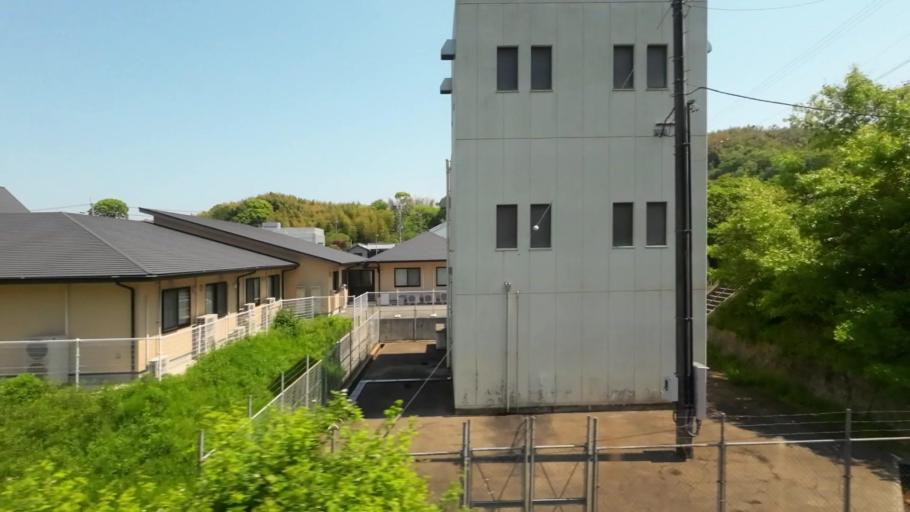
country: JP
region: Ehime
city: Hojo
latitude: 34.0946
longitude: 132.9741
